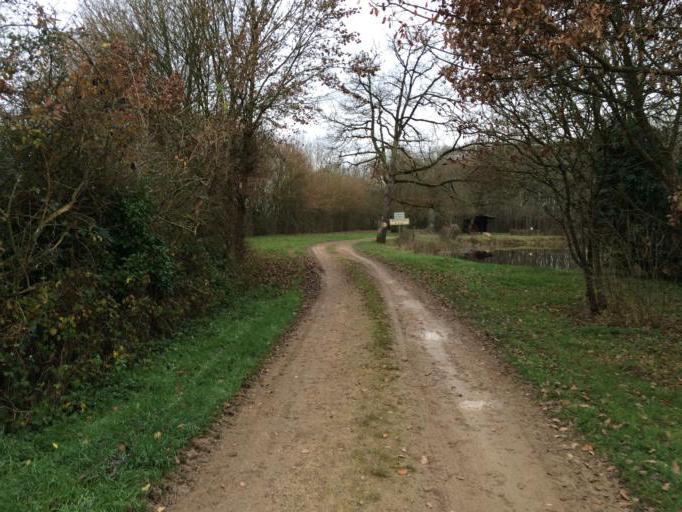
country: FR
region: Poitou-Charentes
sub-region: Departement des Deux-Sevres
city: Sauze-Vaussais
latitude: 46.1653
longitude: 0.1216
